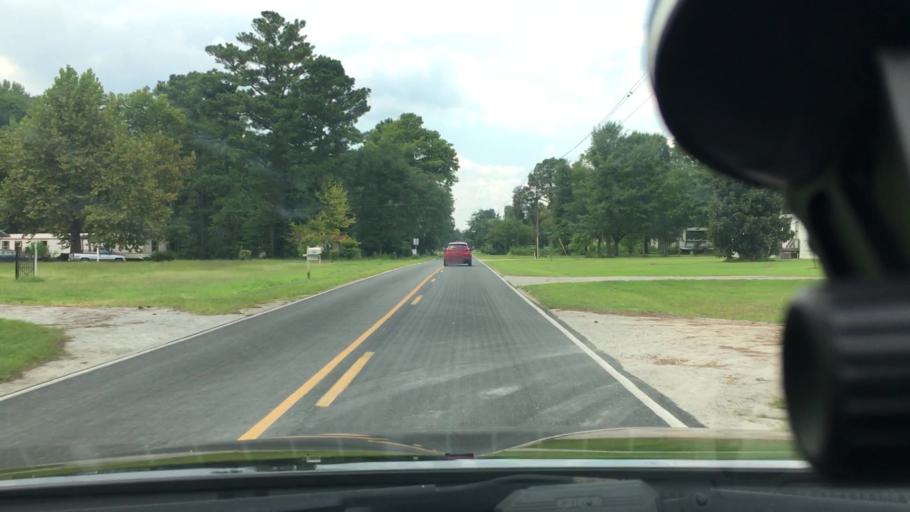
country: US
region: North Carolina
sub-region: Craven County
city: New Bern
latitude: 35.1744
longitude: -77.0521
